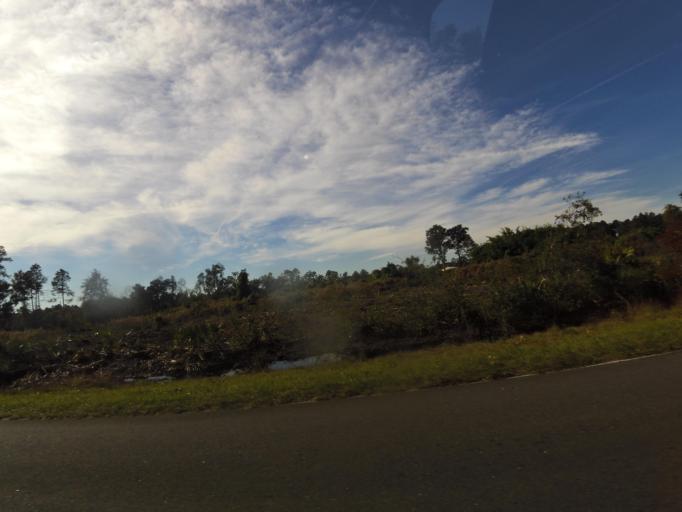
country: US
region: Georgia
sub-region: Glynn County
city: Brunswick
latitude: 31.1340
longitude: -81.5565
